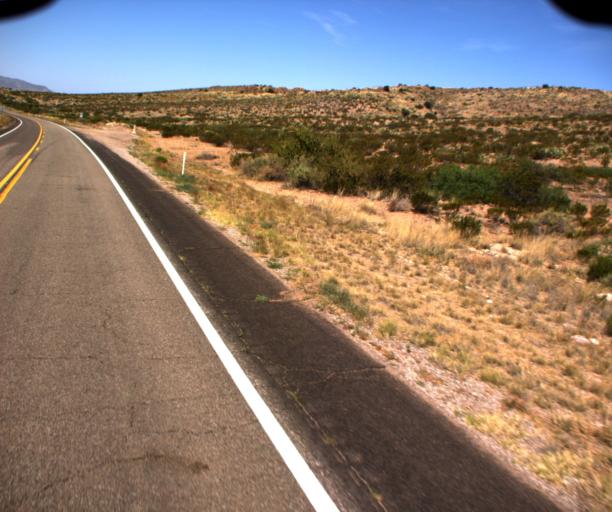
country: US
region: Arizona
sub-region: Greenlee County
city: Clifton
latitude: 32.7743
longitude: -109.3106
